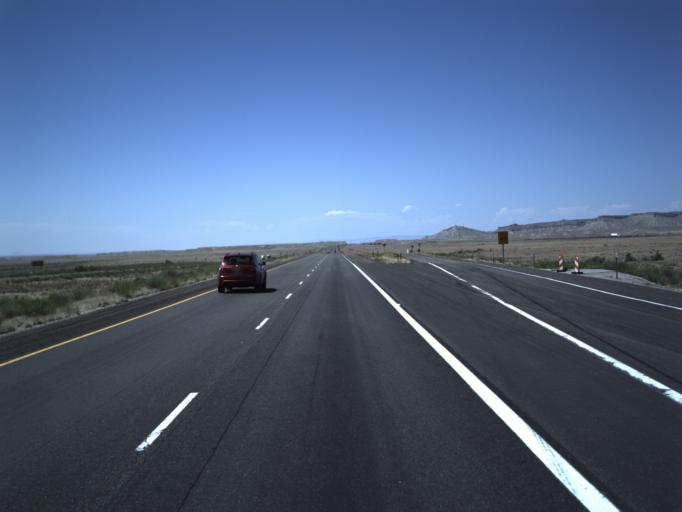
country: US
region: Utah
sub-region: Grand County
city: Moab
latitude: 38.9568
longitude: -109.7479
